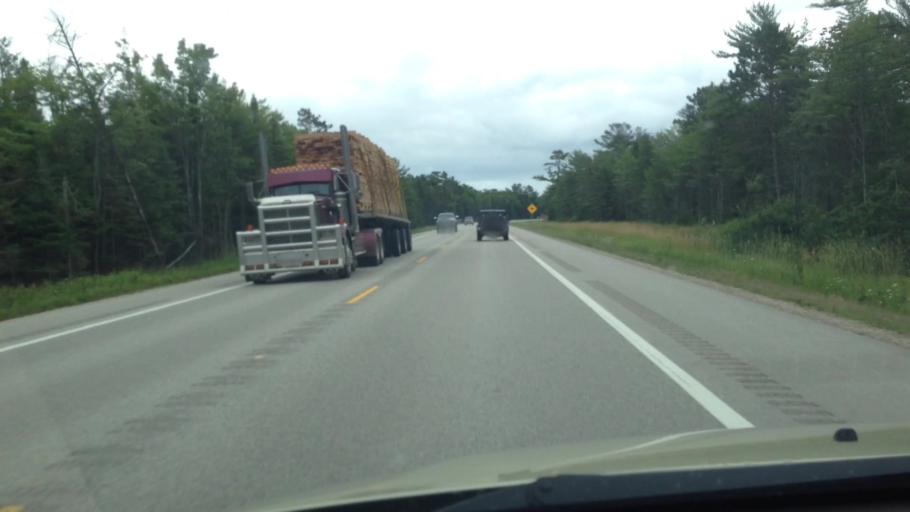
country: US
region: Michigan
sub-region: Luce County
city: Newberry
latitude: 46.0989
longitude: -85.4842
